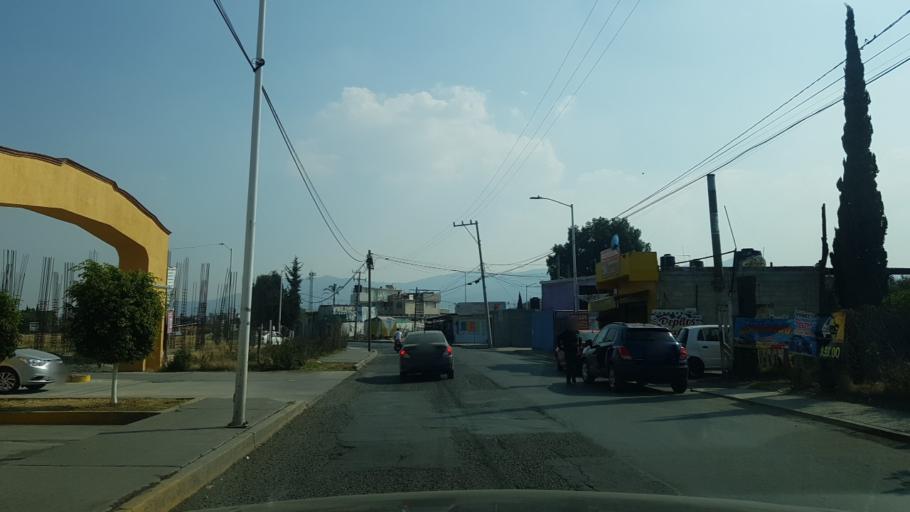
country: MX
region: Mexico
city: Santiago Teyahualco
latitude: 19.6602
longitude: -99.1278
